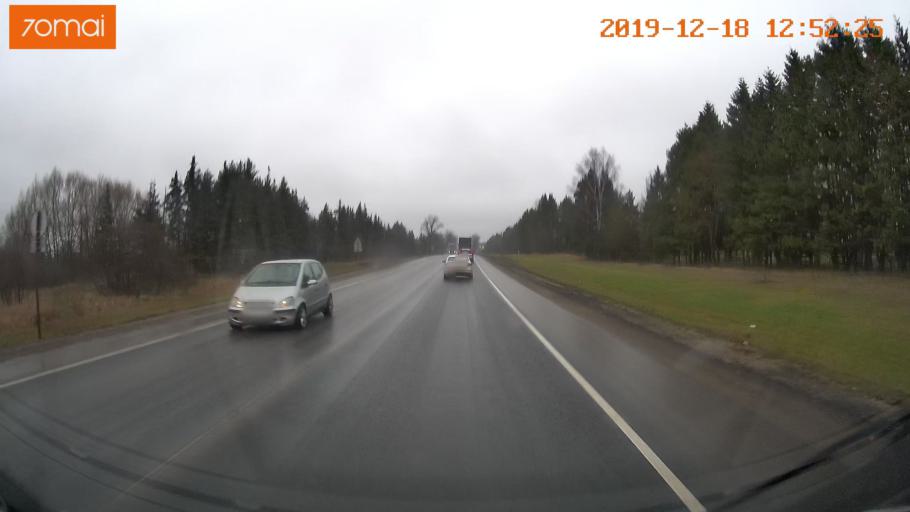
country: RU
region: Moskovskaya
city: Klin
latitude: 56.3112
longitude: 36.6875
